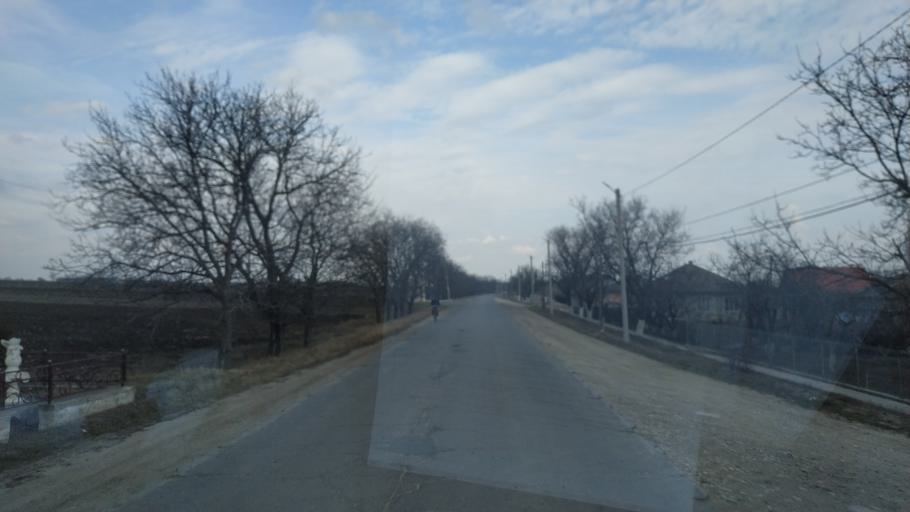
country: MD
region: Anenii Noi
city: Anenii Noi
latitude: 46.8964
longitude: 29.3063
